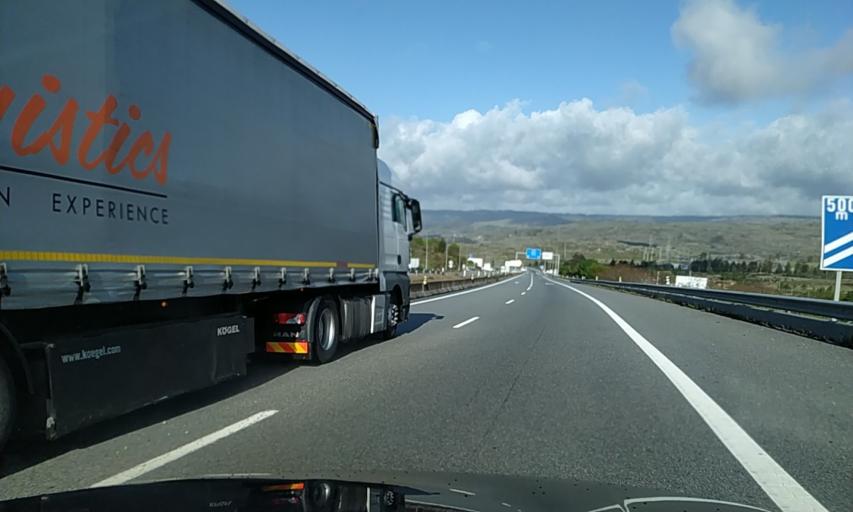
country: PT
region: Guarda
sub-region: Celorico da Beira
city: Celorico da Beira
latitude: 40.6277
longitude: -7.4081
